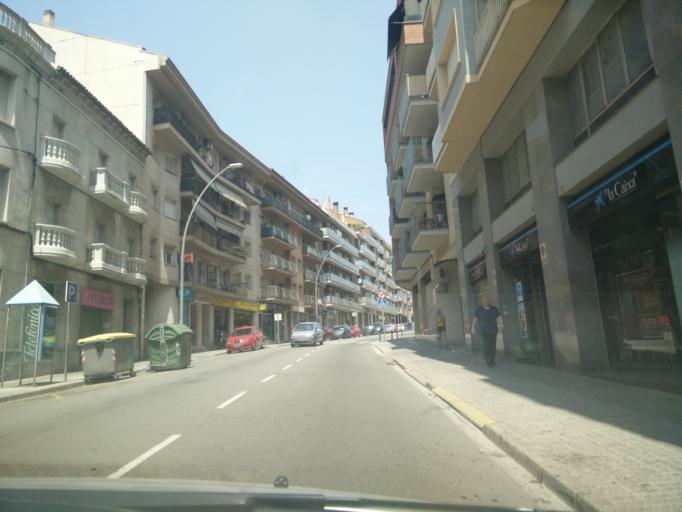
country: ES
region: Catalonia
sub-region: Provincia de Barcelona
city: Manresa
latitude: 41.7334
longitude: 1.8227
